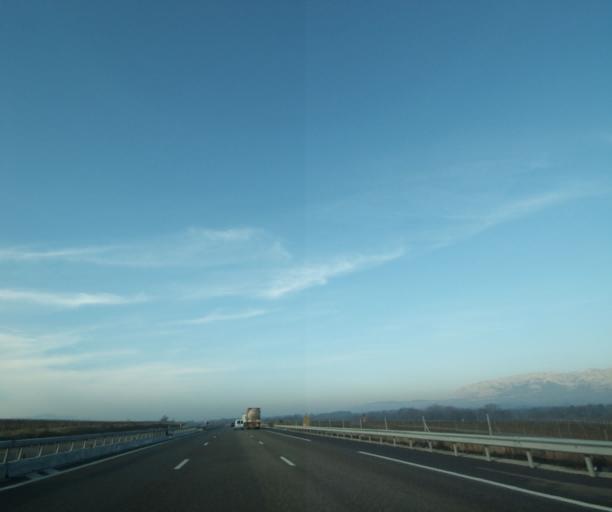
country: FR
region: Provence-Alpes-Cote d'Azur
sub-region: Departement du Var
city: Pourrieres
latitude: 43.4774
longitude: 5.7137
